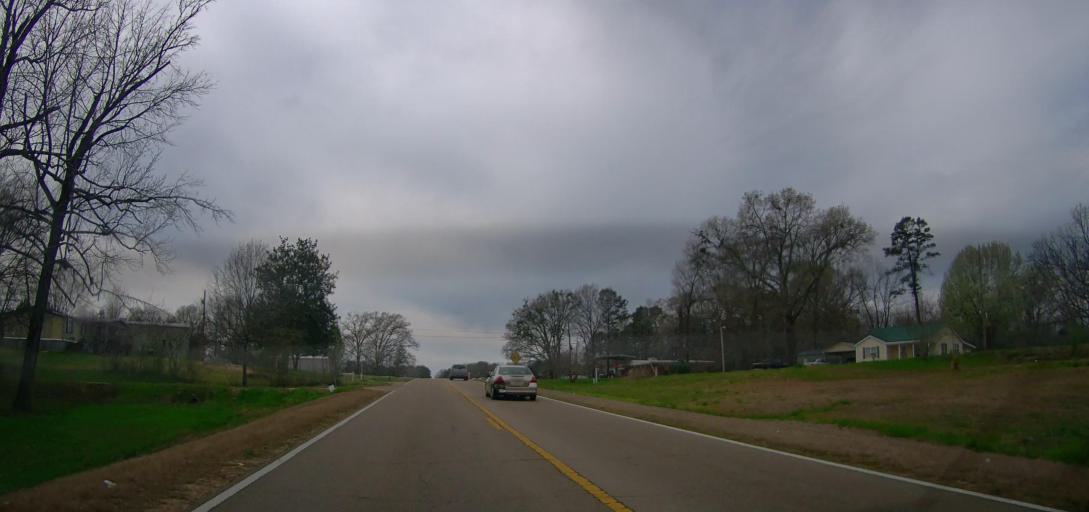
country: US
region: Mississippi
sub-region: Itawamba County
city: Mantachie
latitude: 34.2546
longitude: -88.4880
